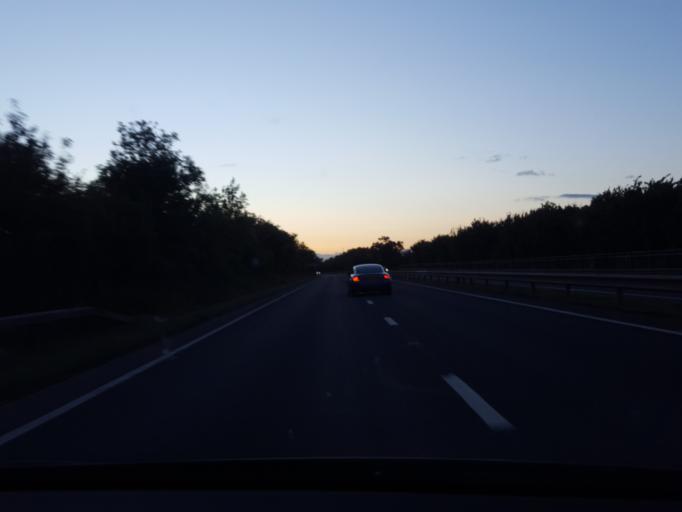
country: GB
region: England
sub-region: Leicestershire
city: Barrow upon Soar
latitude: 52.7464
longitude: -1.1553
